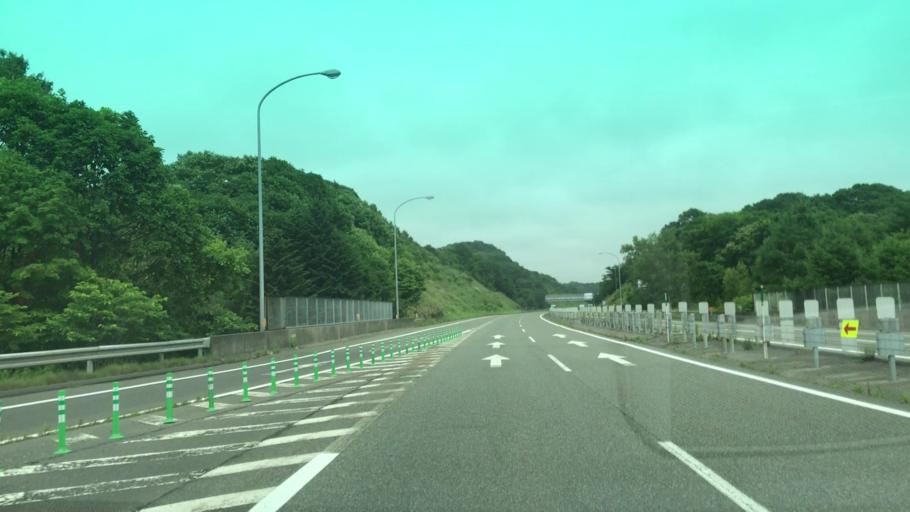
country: JP
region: Hokkaido
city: Tomakomai
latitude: 42.6330
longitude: 141.4900
